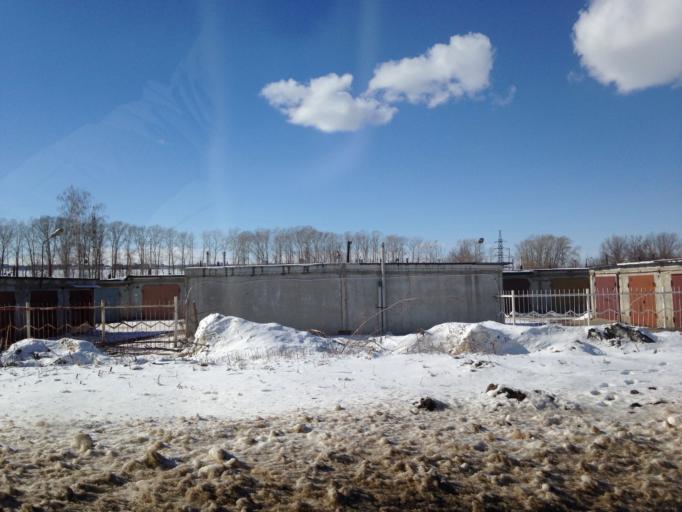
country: RU
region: Ulyanovsk
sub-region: Ulyanovskiy Rayon
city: Ulyanovsk
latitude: 54.3242
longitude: 48.4706
